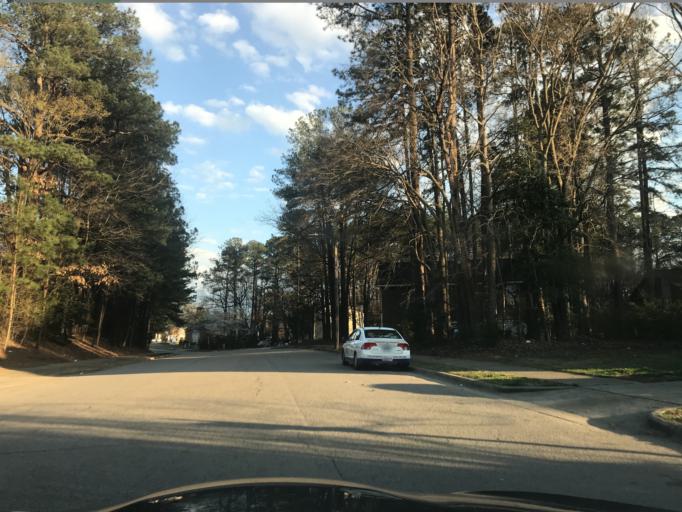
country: US
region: North Carolina
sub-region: Wake County
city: Raleigh
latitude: 35.8401
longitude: -78.5944
